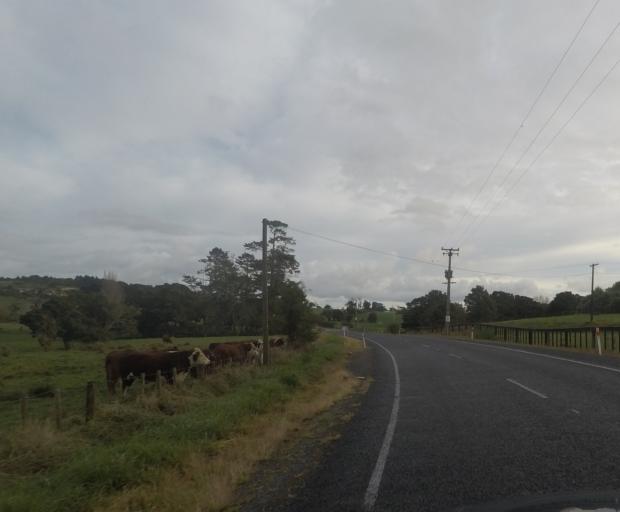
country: NZ
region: Auckland
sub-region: Auckland
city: Wellsford
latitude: -36.2145
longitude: 174.5869
